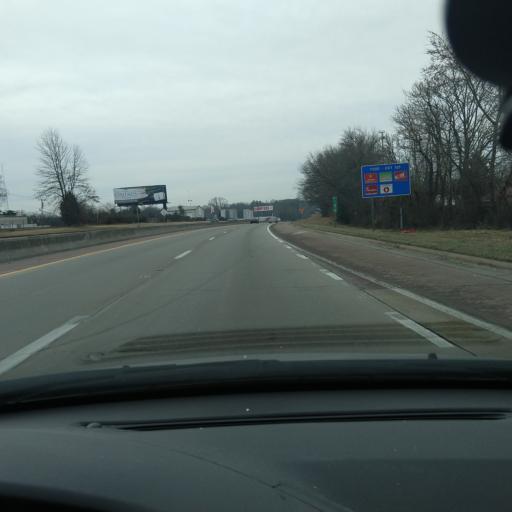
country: US
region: North Carolina
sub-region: Forsyth County
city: Winston-Salem
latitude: 36.0583
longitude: -80.2319
